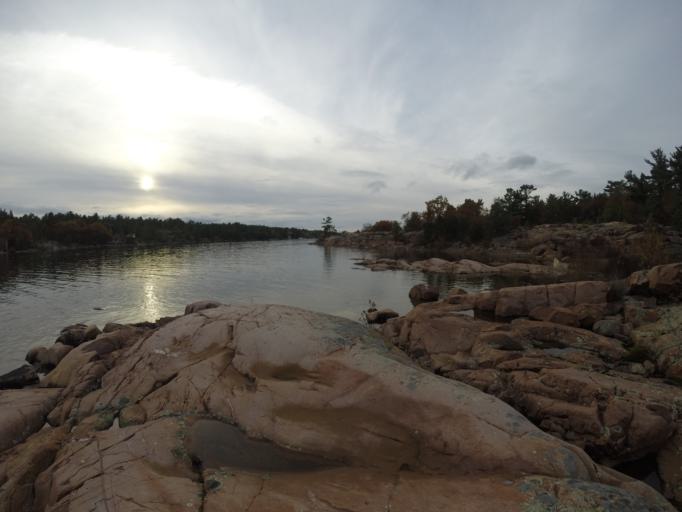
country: CA
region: Ontario
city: Espanola
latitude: 45.9683
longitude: -81.5004
